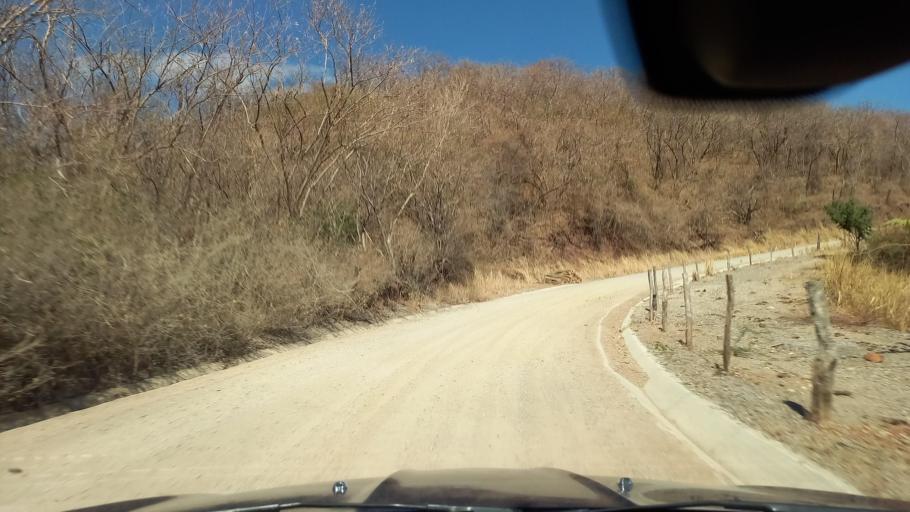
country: SV
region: Santa Ana
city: Metapan
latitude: 14.3592
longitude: -89.4809
